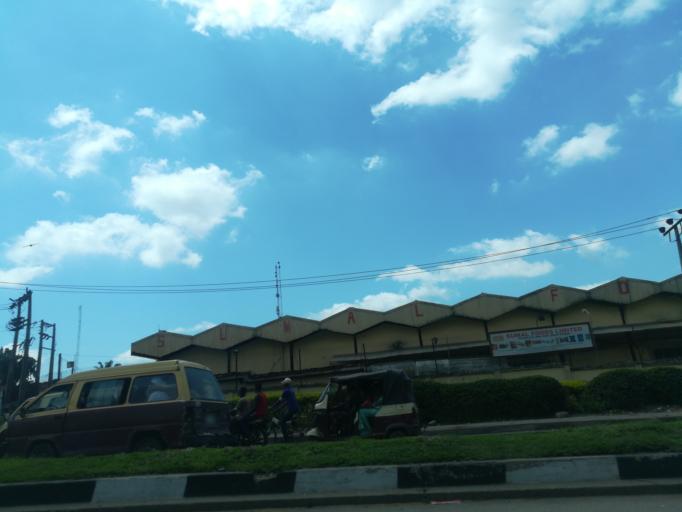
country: NG
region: Oyo
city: Ibadan
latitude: 7.3701
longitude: 3.8600
